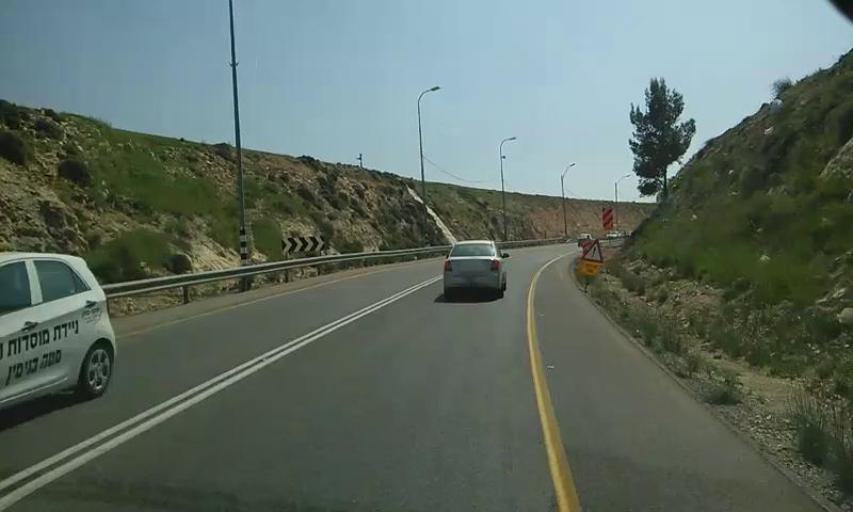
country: PS
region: West Bank
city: Jaba`
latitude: 31.8573
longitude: 35.2664
